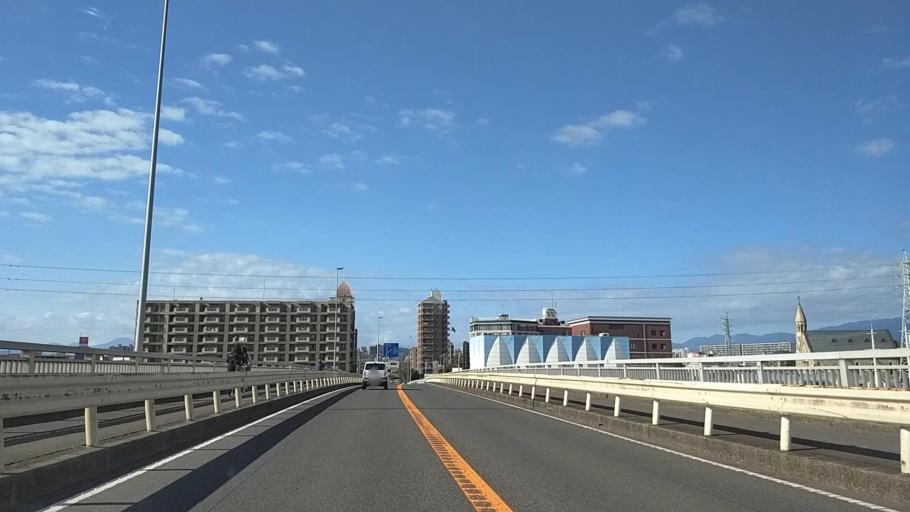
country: JP
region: Kanagawa
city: Hiratsuka
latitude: 35.3317
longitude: 139.3662
